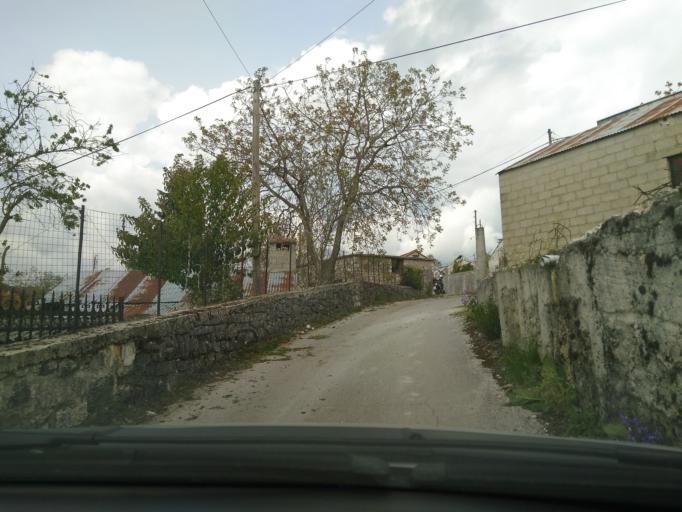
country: GR
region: Epirus
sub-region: Nomos Ioanninon
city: Asprangeloi
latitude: 39.7786
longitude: 20.6887
